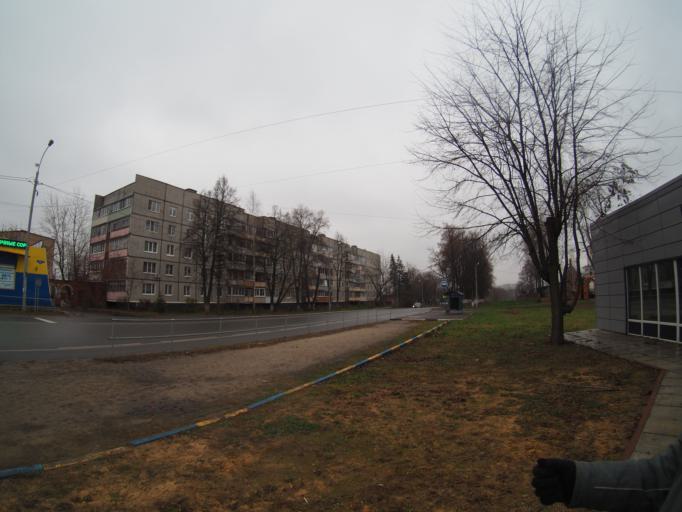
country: RU
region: Moskovskaya
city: Mikhnevo
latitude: 55.1185
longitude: 37.9466
